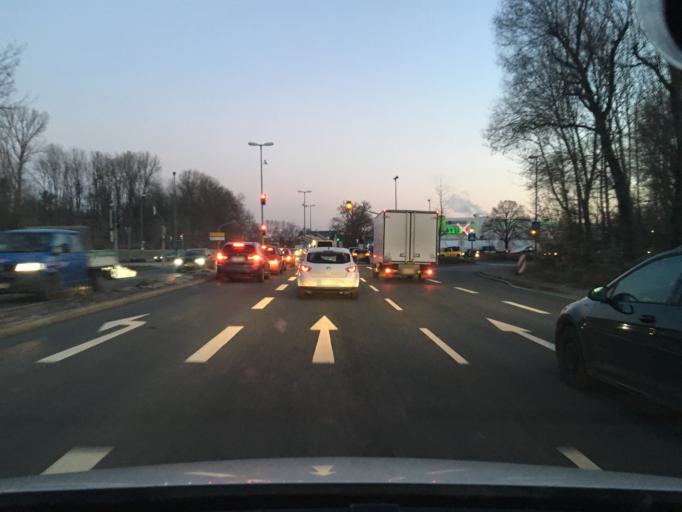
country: DE
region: Bavaria
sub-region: Upper Bavaria
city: Rosenheim
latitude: 47.8387
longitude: 12.1216
